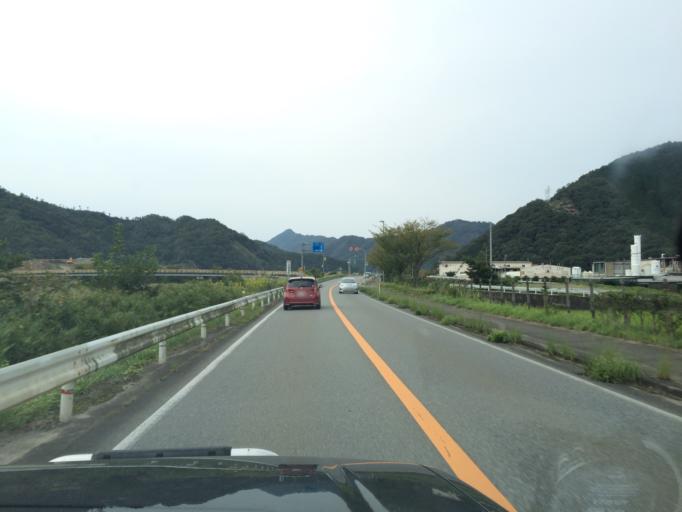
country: JP
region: Hyogo
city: Toyooka
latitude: 35.3912
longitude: 134.7970
